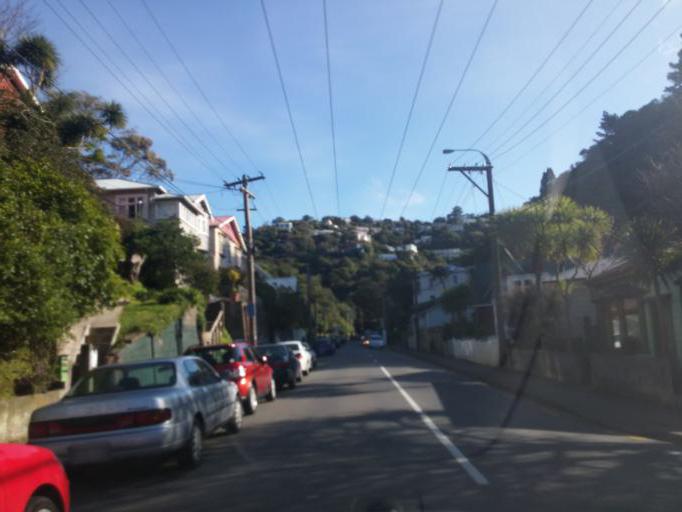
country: NZ
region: Wellington
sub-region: Wellington City
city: Kelburn
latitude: -41.2945
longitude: 174.7629
